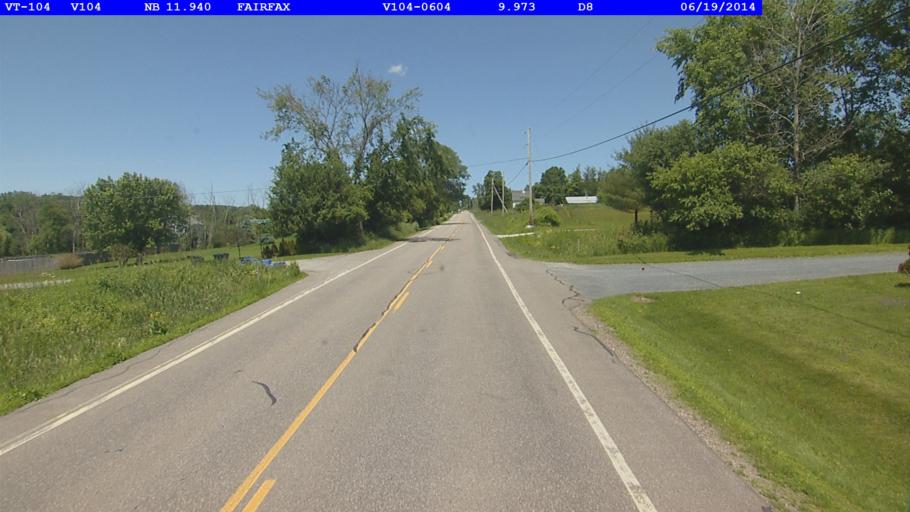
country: US
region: Vermont
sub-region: Franklin County
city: Saint Albans
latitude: 44.7278
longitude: -73.0453
